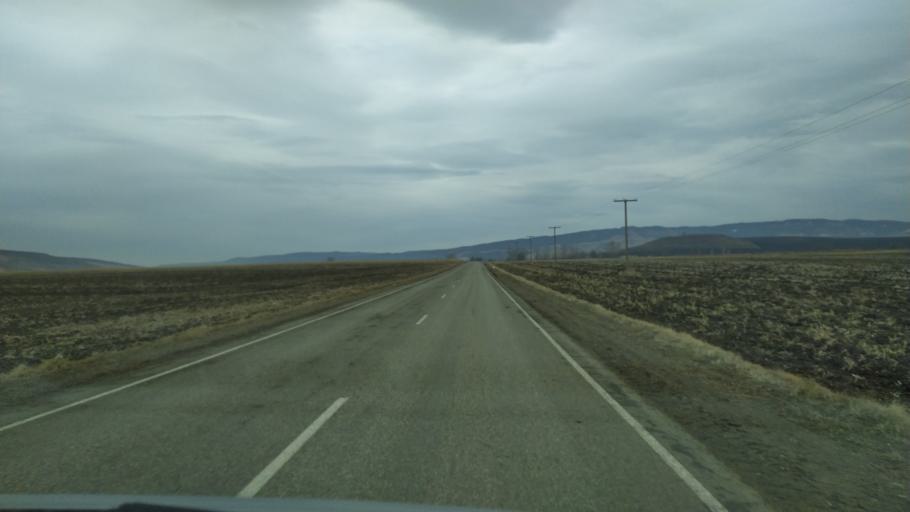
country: RU
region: Krasnodarskiy
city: Peredovaya
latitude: 44.1098
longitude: 41.4397
